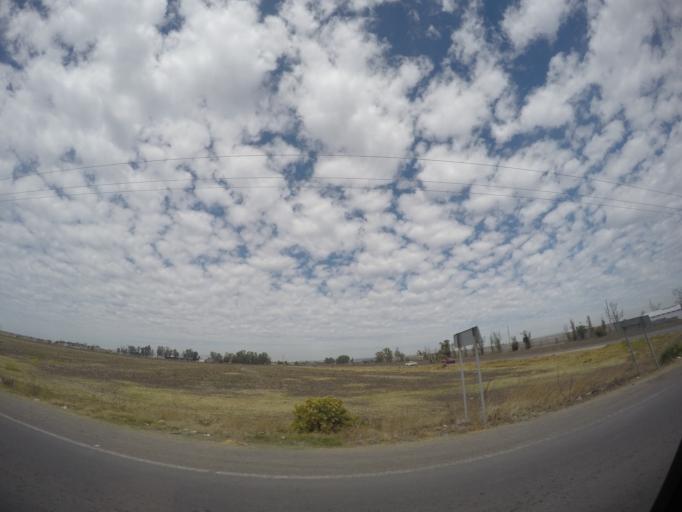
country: MX
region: Guanajuato
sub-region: Leon
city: Colonia Latinoamericana
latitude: 21.0345
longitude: -101.6943
